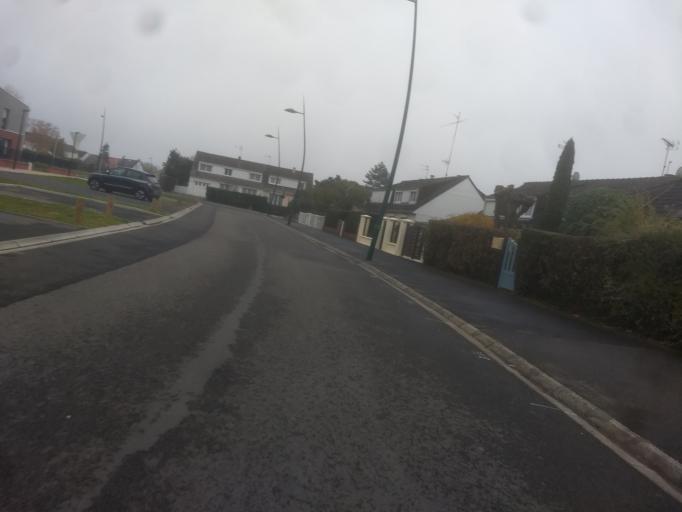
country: FR
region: Nord-Pas-de-Calais
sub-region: Departement du Pas-de-Calais
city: Saint-Laurent-Blangy
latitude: 50.3043
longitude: 2.7956
